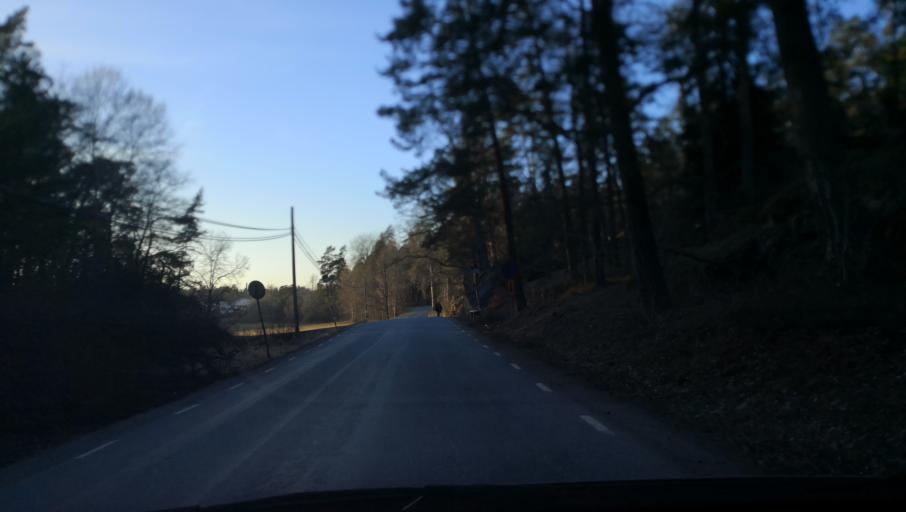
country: SE
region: Stockholm
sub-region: Varmdo Kommun
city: Gustavsberg
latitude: 59.3287
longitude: 18.4122
